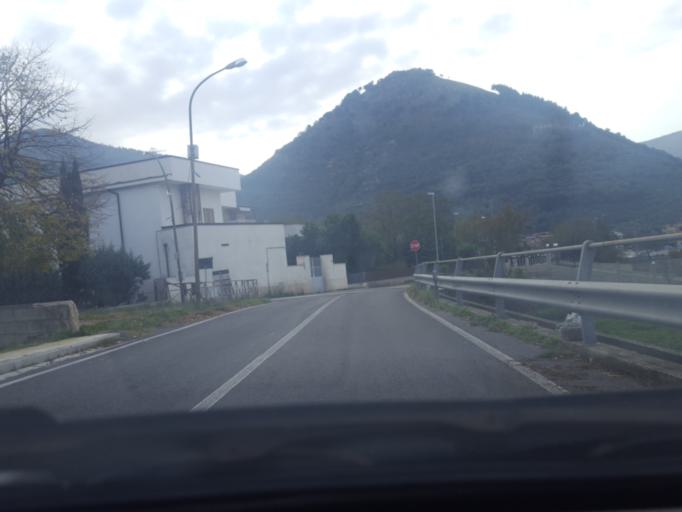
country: IT
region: Campania
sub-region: Provincia di Caserta
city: Arienzo
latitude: 41.0258
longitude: 14.4914
